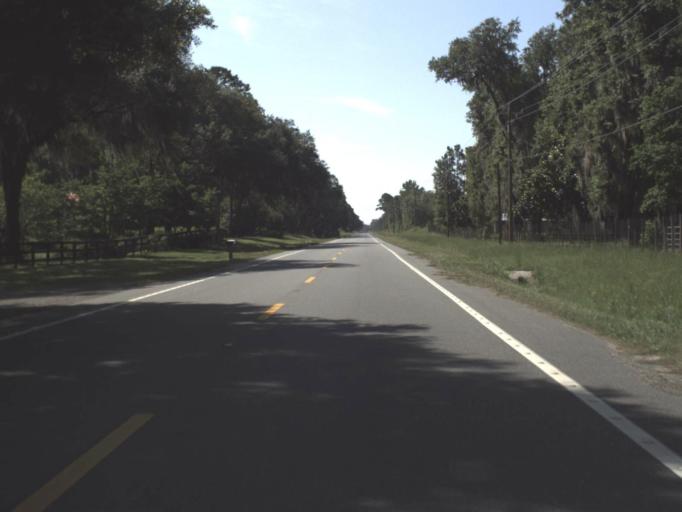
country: US
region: Florida
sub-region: Madison County
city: Madison
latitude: 30.4266
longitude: -83.3838
